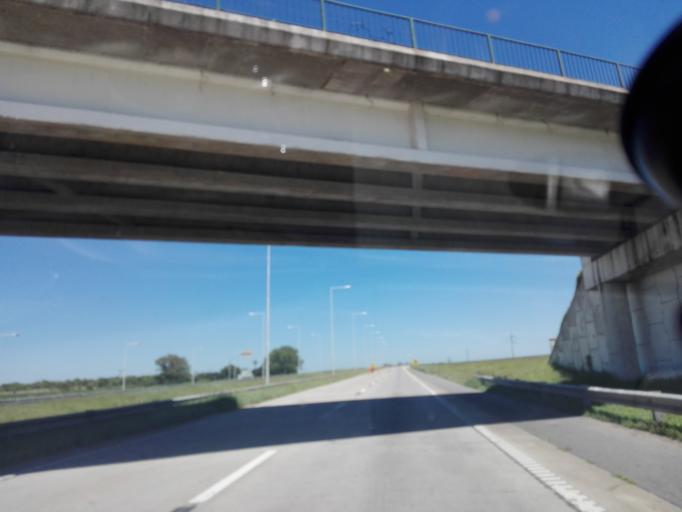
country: AR
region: Santa Fe
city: Canada de Gomez
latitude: -32.8551
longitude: -61.3401
